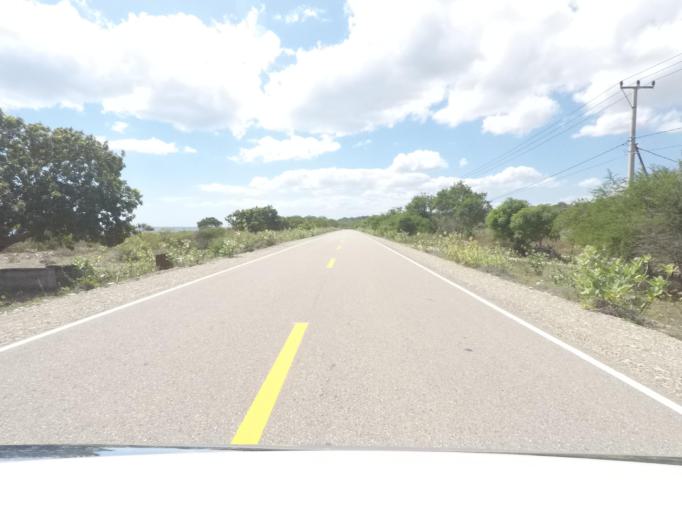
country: TL
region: Baucau
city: Baucau
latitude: -8.4198
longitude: 126.7084
